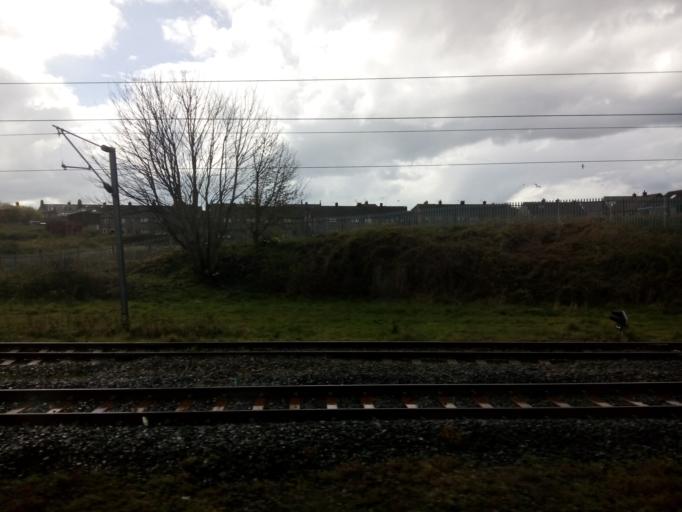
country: GB
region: England
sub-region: Northumberland
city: Berwick-Upon-Tweed
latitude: 55.7785
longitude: -2.0075
